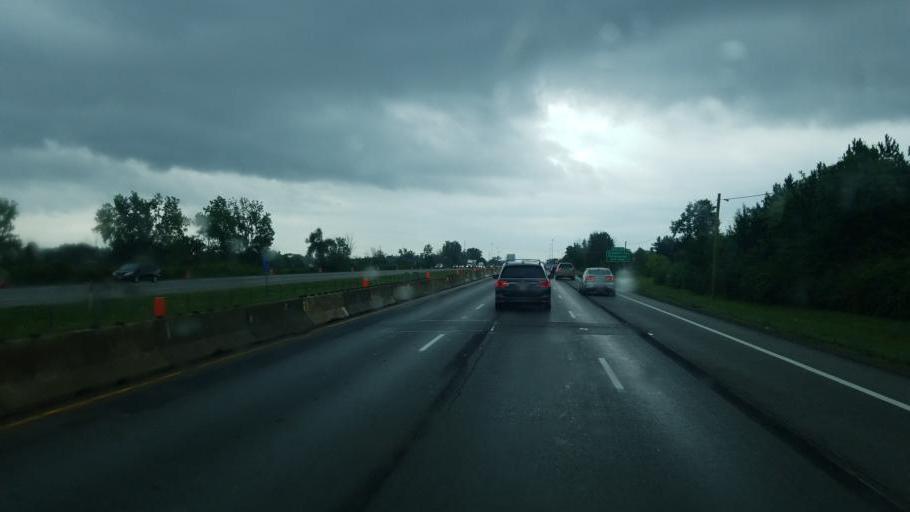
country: US
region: Ohio
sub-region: Franklin County
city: Hilliard
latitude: 40.0472
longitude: -83.1279
